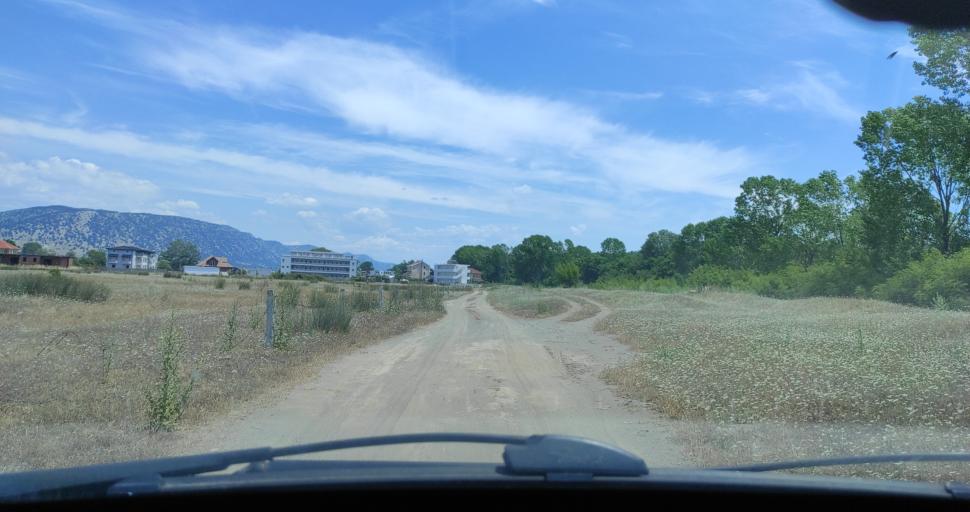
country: AL
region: Shkoder
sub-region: Rrethi i Shkodres
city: Velipoje
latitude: 41.8694
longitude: 19.3972
